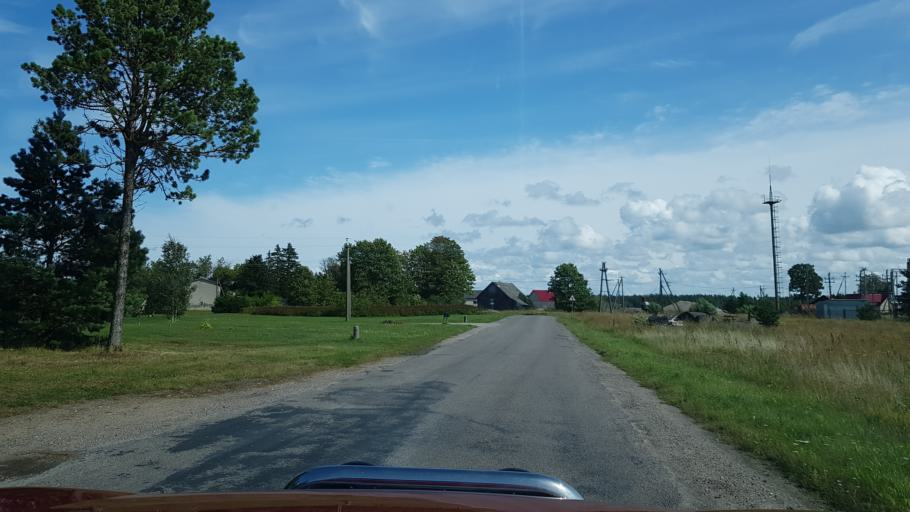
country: EE
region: Laeaene
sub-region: Lihula vald
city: Lihula
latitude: 58.4511
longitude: 23.7418
